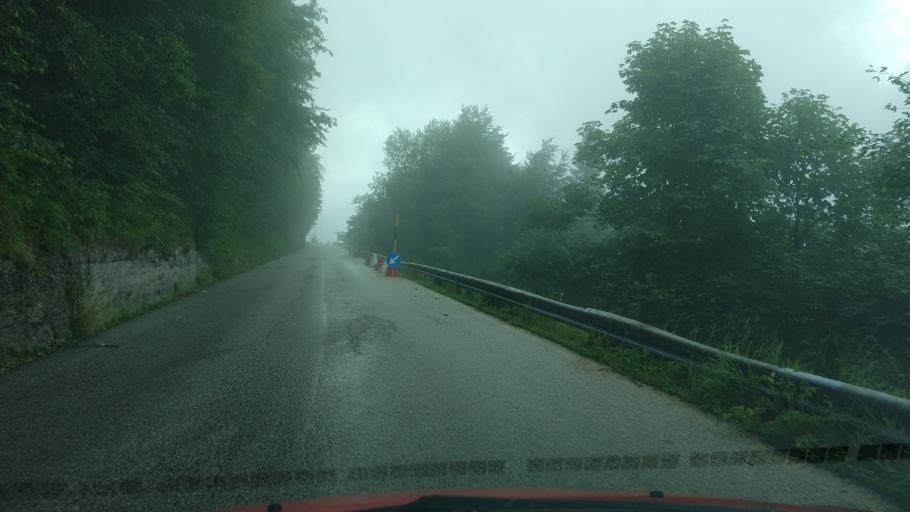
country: IT
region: Veneto
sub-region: Provincia di Vicenza
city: Longhi
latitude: 45.8768
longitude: 11.3059
